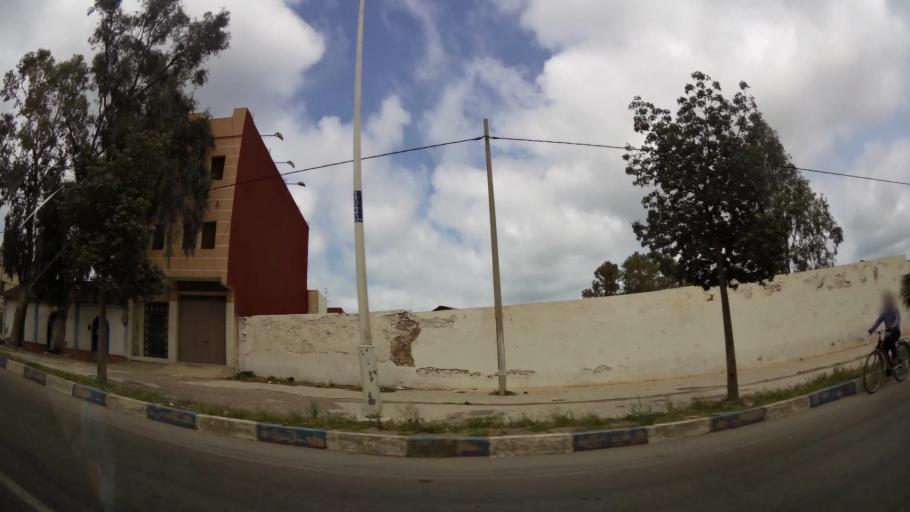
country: MA
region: Oriental
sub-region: Nador
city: Nador
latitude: 35.1862
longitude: -2.9283
